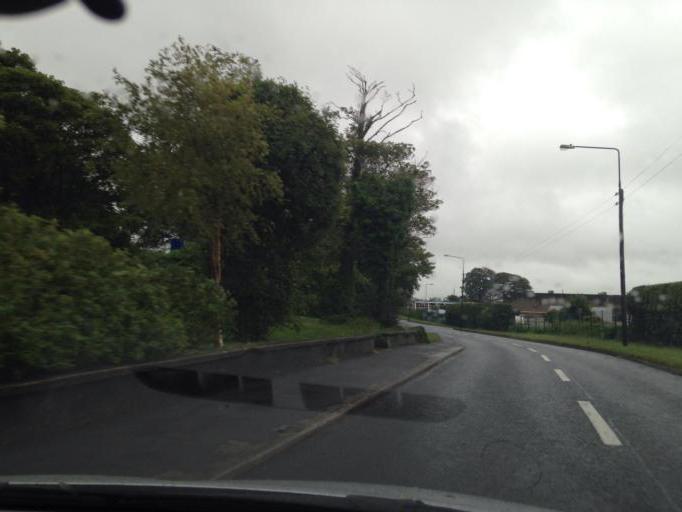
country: IE
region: Connaught
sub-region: County Galway
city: Gaillimh
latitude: 53.2854
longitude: -9.0226
